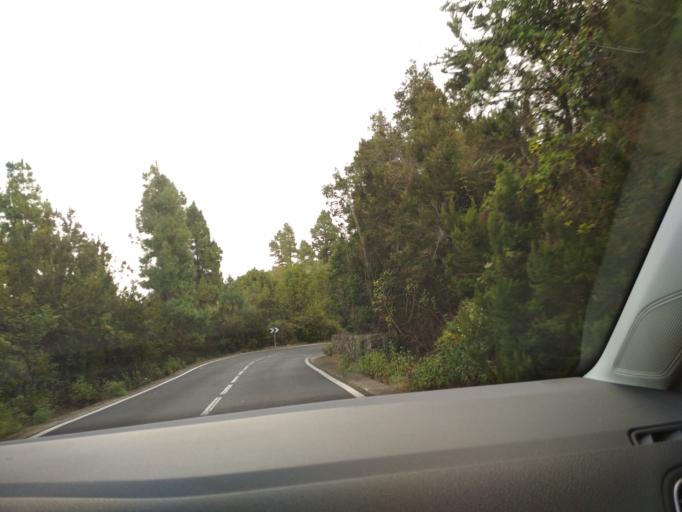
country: ES
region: Canary Islands
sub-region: Provincia de Santa Cruz de Tenerife
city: Garachico
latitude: 28.3430
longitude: -16.7544
